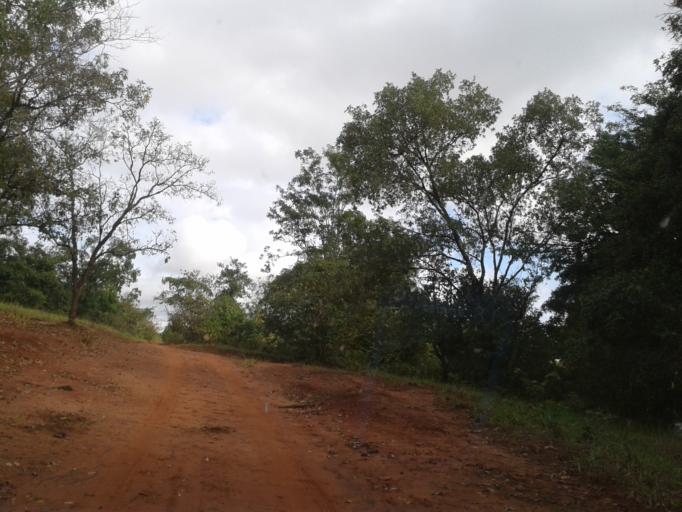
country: BR
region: Minas Gerais
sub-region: Campina Verde
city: Campina Verde
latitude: -19.4922
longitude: -49.6080
